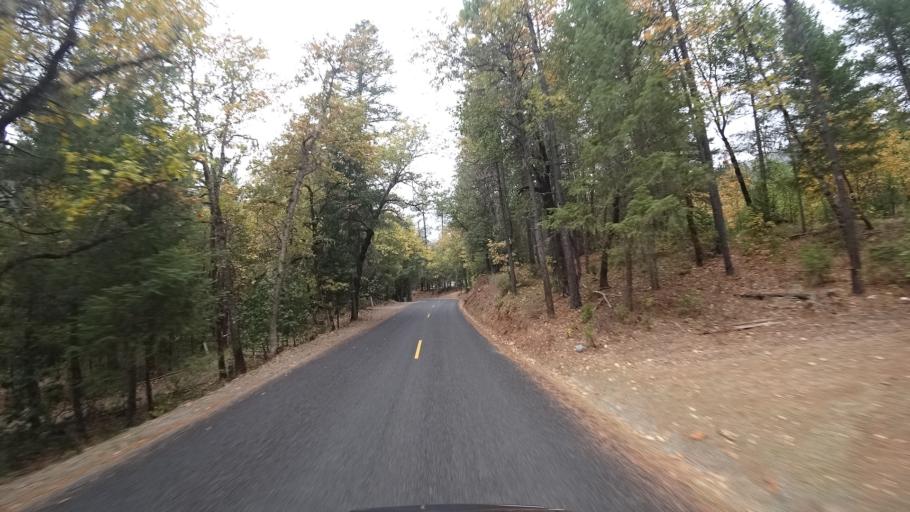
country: US
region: California
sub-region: Siskiyou County
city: Happy Camp
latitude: 41.8509
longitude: -123.1769
